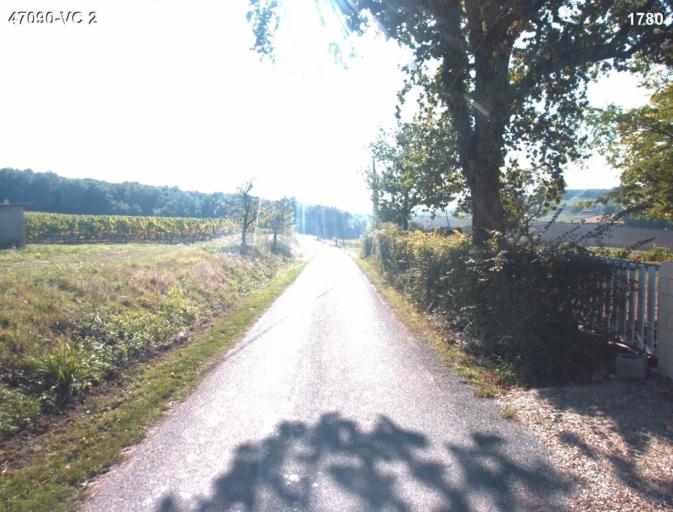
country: FR
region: Aquitaine
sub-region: Departement du Lot-et-Garonne
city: Nerac
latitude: 44.1782
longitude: 0.3738
